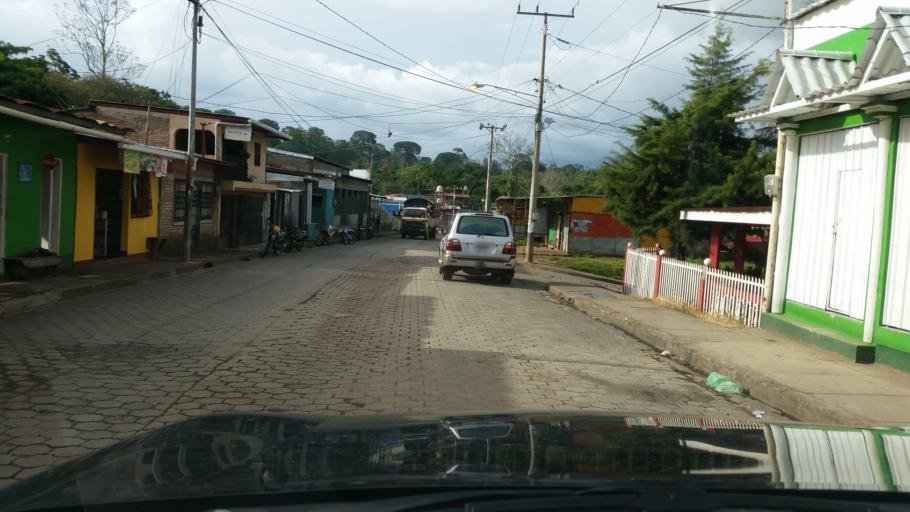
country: NI
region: Matagalpa
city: San Ramon
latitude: 13.1411
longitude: -85.7350
